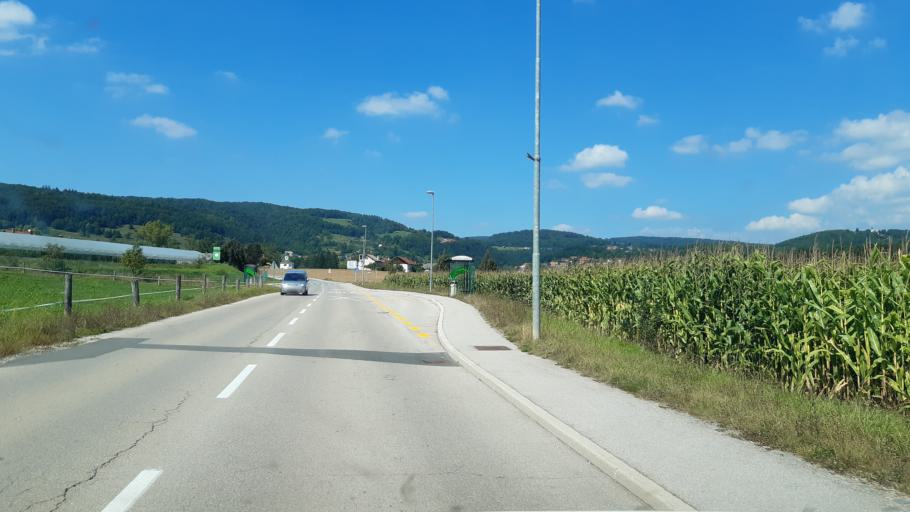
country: SI
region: Ivancna Gorica
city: Ivancna Gorica
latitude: 45.9443
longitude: 14.8034
